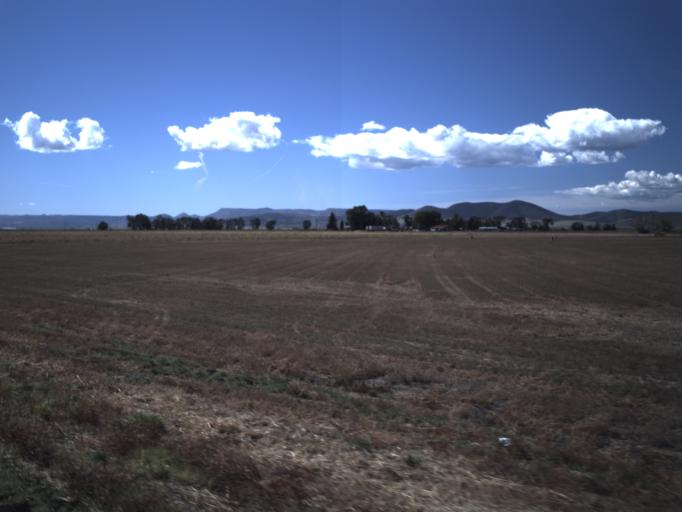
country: US
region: Utah
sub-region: Washington County
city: Enterprise
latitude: 37.7013
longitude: -113.6565
